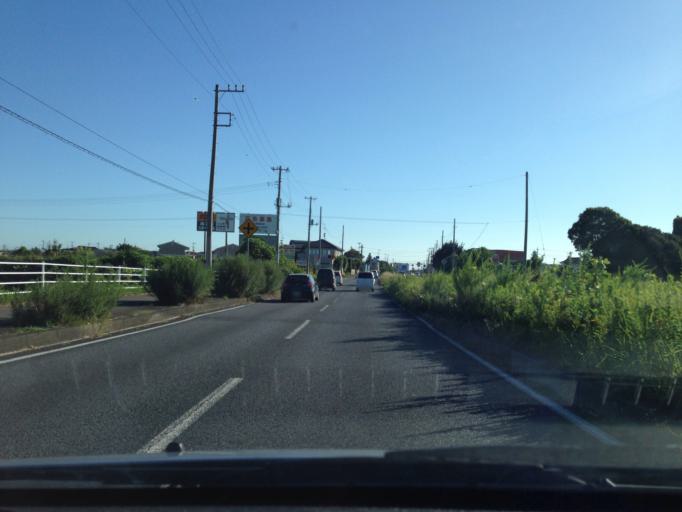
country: JP
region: Ibaraki
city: Naka
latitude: 36.0427
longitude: 140.1809
